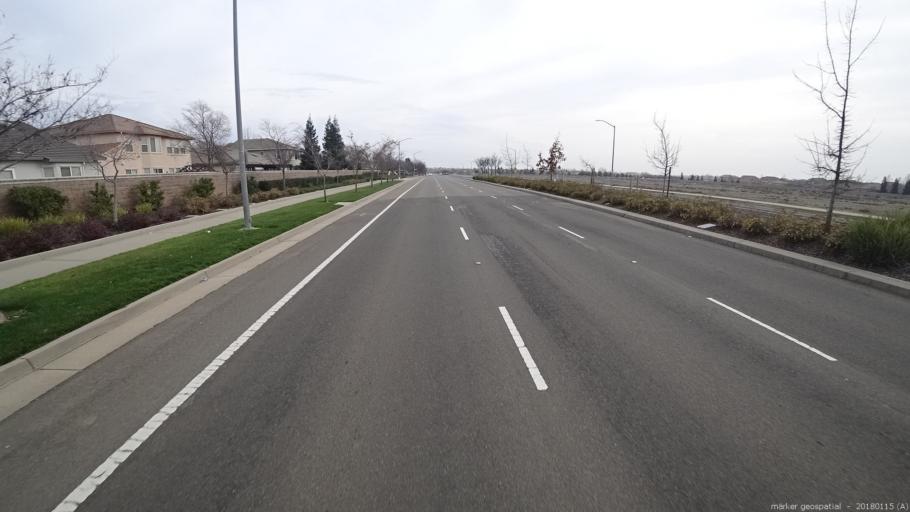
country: US
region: California
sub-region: Sacramento County
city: Rancho Cordova
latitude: 38.5784
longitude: -121.2806
